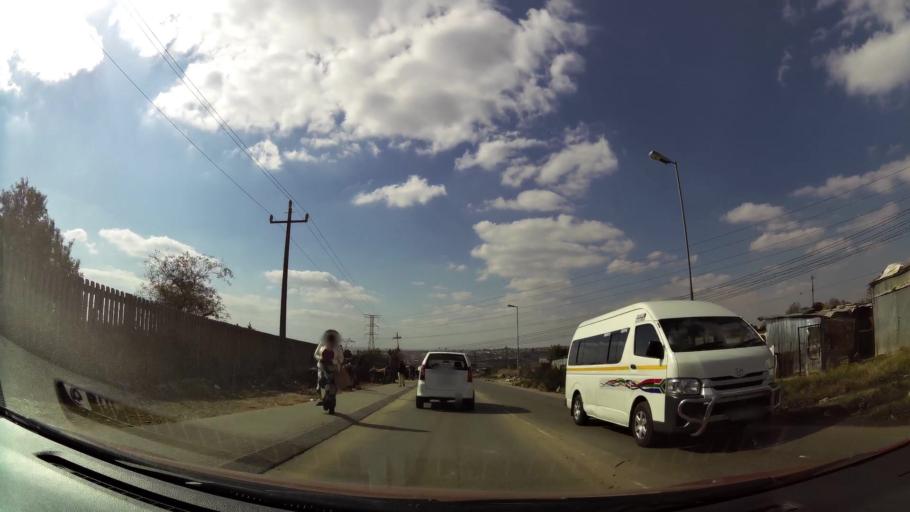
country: ZA
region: Gauteng
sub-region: Ekurhuleni Metropolitan Municipality
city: Tembisa
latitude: -26.0046
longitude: 28.1856
